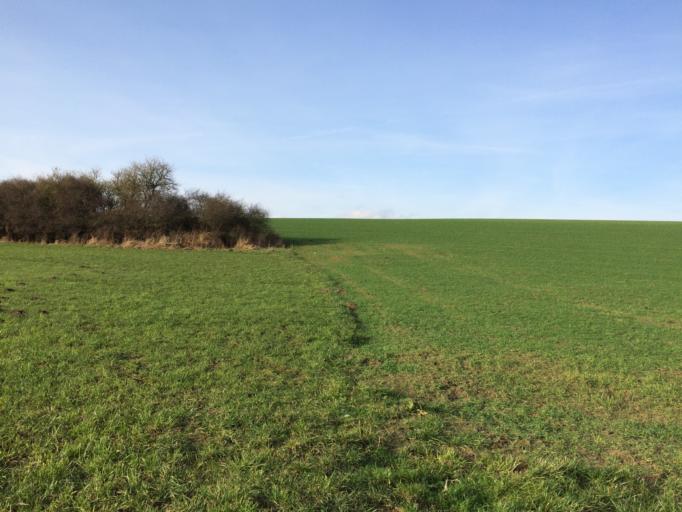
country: DE
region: North Rhine-Westphalia
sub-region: Regierungsbezirk Detmold
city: Blomberg
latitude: 51.9203
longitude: 9.1335
